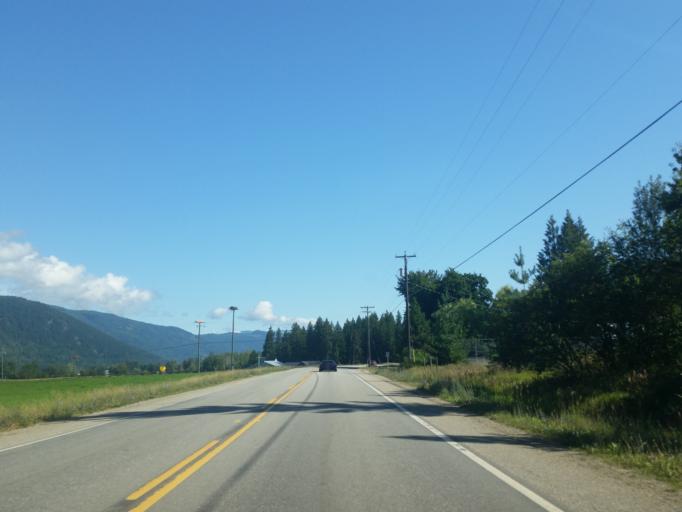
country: CA
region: British Columbia
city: Enderby
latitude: 50.6796
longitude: -119.0542
